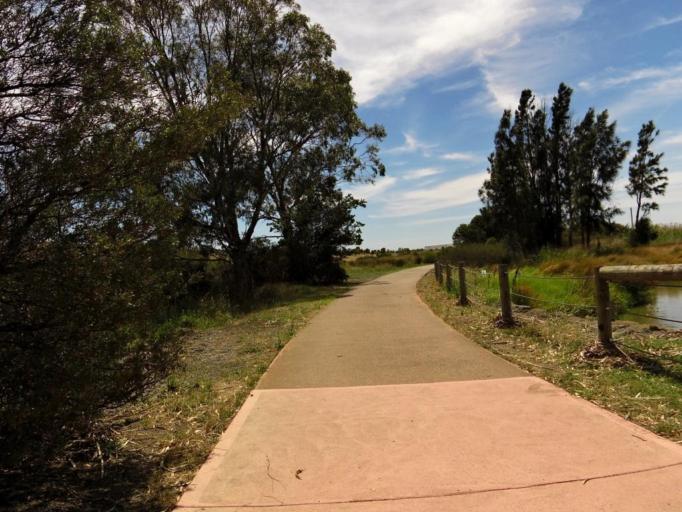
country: AU
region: Victoria
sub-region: Hobsons Bay
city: Altona
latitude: -37.8580
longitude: 144.8266
